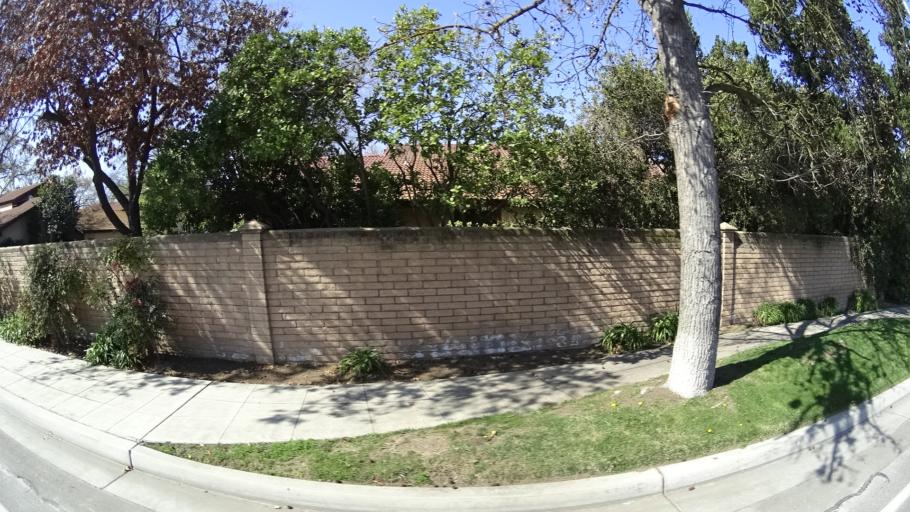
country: US
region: California
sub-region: Fresno County
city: Fresno
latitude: 36.8208
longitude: -119.8265
